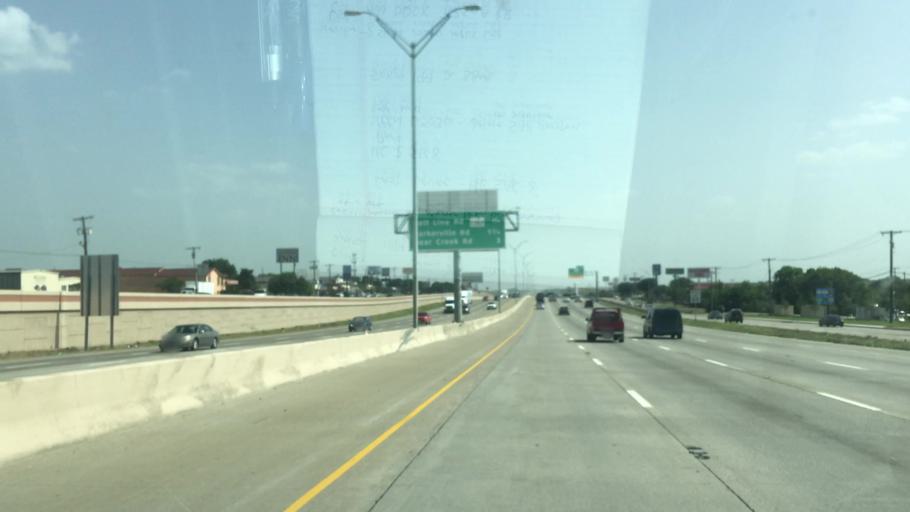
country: US
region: Texas
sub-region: Dallas County
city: DeSoto
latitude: 32.6133
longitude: -96.8231
